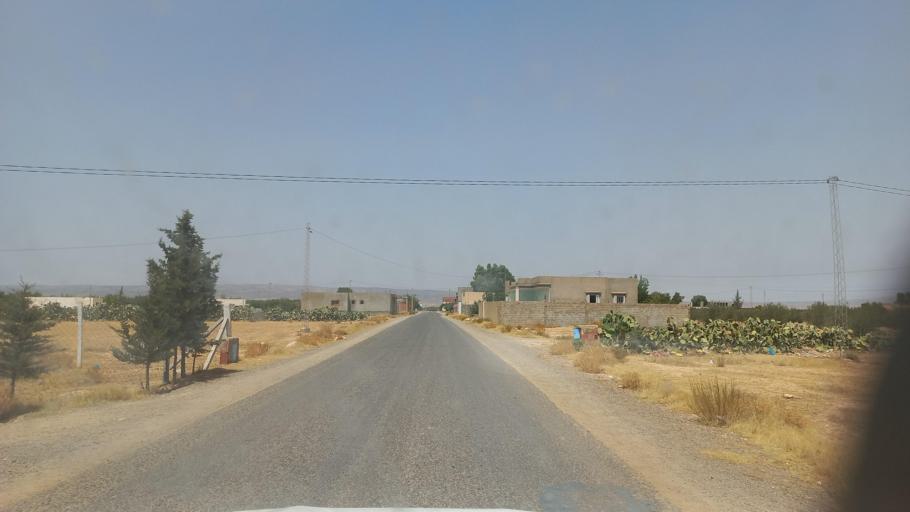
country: TN
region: Al Qasrayn
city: Kasserine
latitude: 35.2513
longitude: 9.0193
